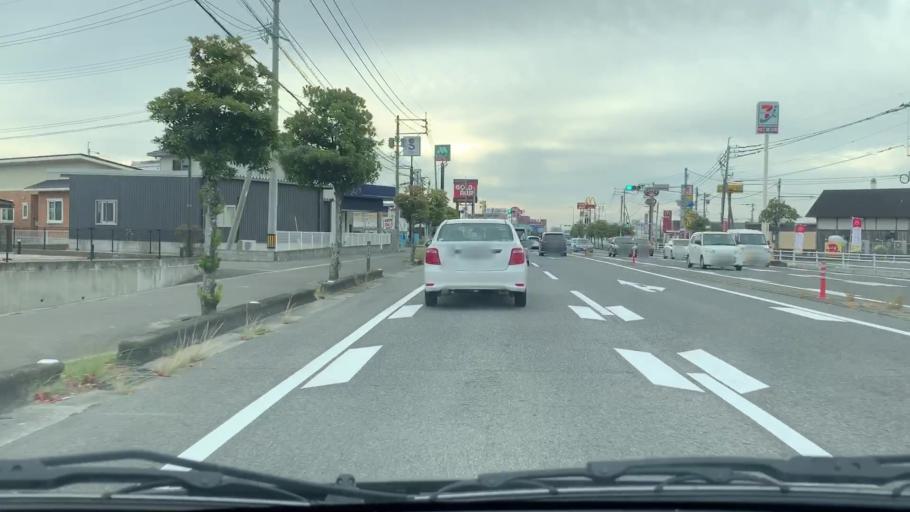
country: JP
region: Saga Prefecture
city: Saga-shi
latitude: 33.2951
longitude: 130.2835
